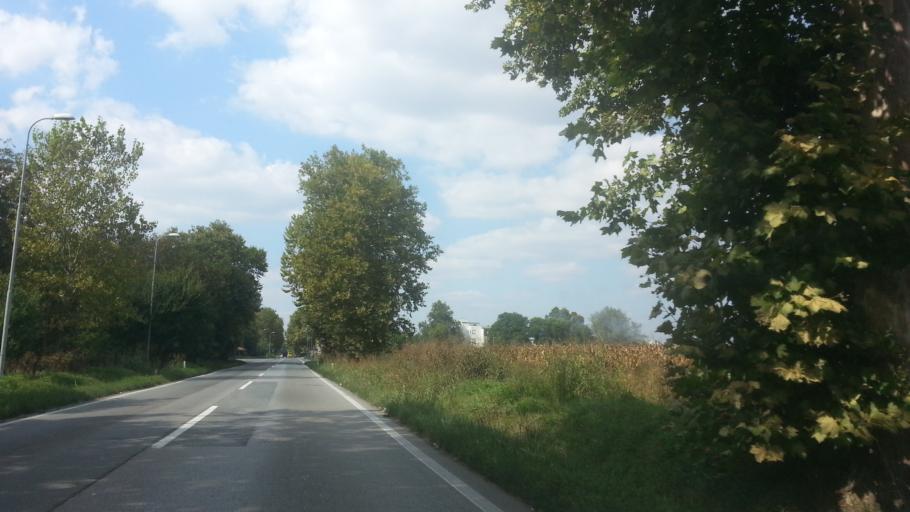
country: RS
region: Central Serbia
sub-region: Belgrade
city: Zemun
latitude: 44.8727
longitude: 20.3466
